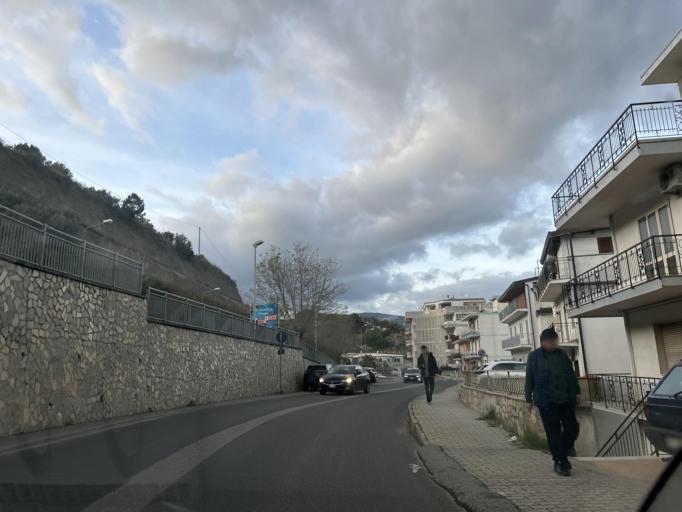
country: IT
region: Calabria
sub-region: Provincia di Catanzaro
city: Soverato Superiore
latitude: 38.6968
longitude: 16.5412
